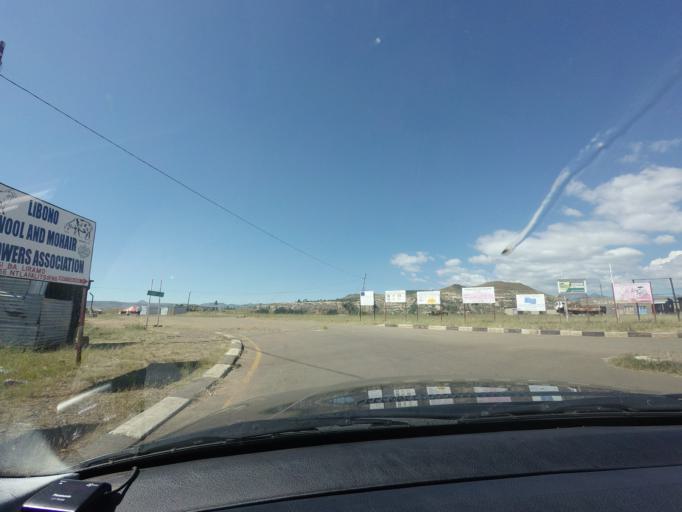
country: LS
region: Butha-Buthe
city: Butha-Buthe
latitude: -28.7041
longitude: 28.3589
